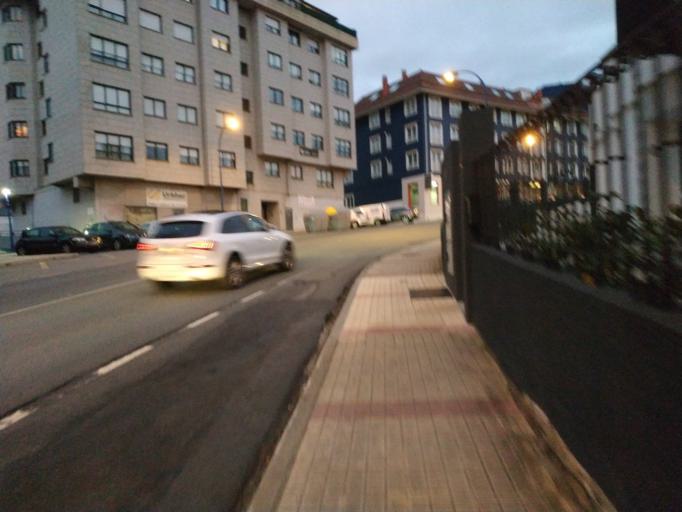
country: ES
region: Galicia
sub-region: Provincia da Coruna
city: Culleredo
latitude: 43.3241
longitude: -8.3841
